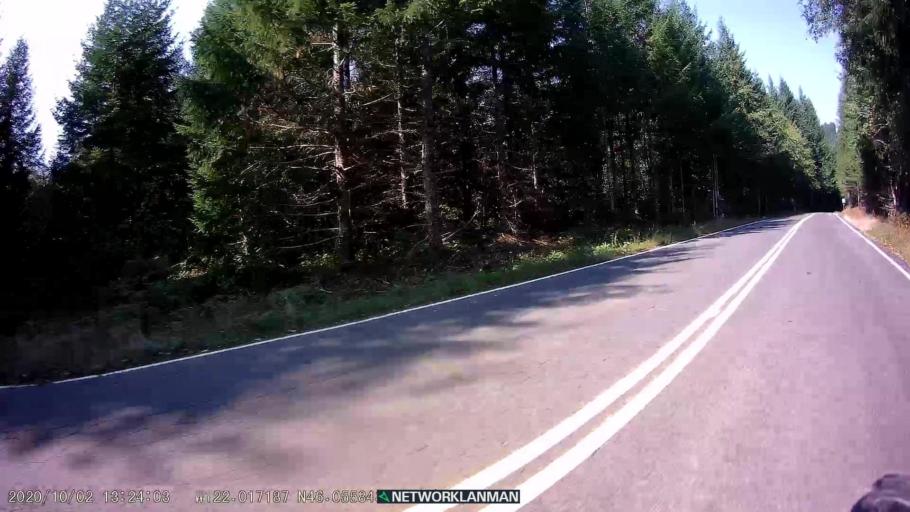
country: US
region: Washington
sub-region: Skamania County
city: Stevenson
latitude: 46.0561
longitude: -122.0172
